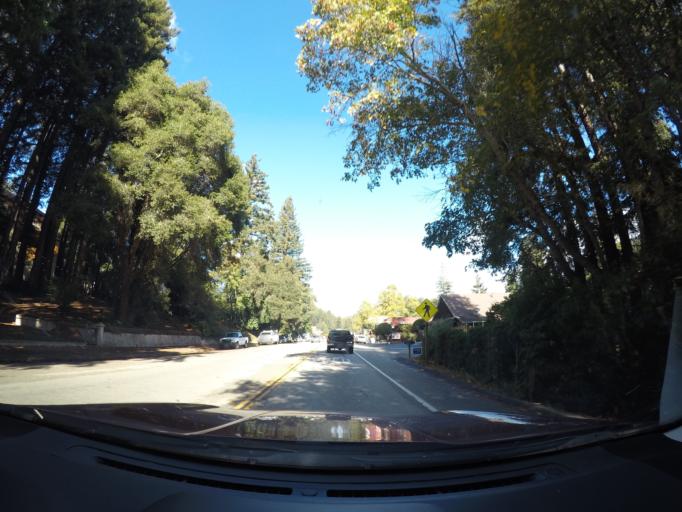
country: US
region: California
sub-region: Santa Cruz County
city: Boulder Creek
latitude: 37.1219
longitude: -122.1212
